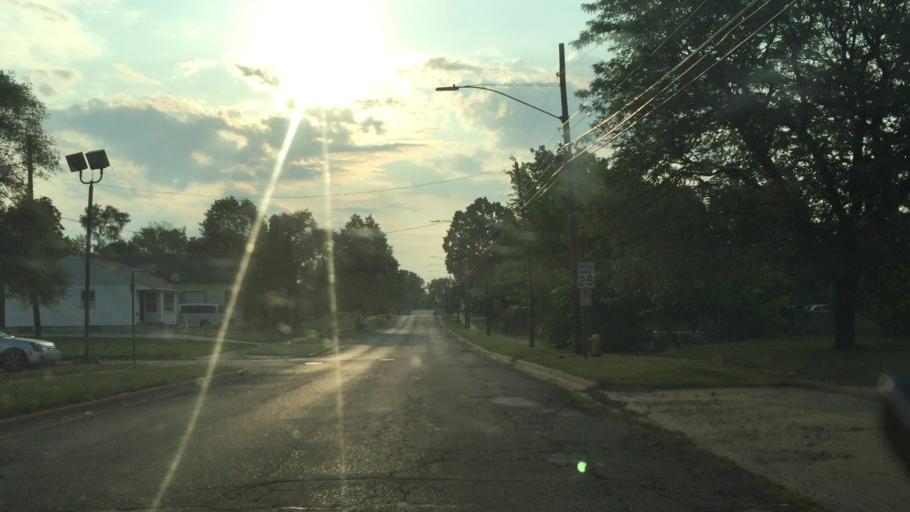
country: US
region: Michigan
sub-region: Oakland County
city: Pontiac
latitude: 42.6380
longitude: -83.2745
